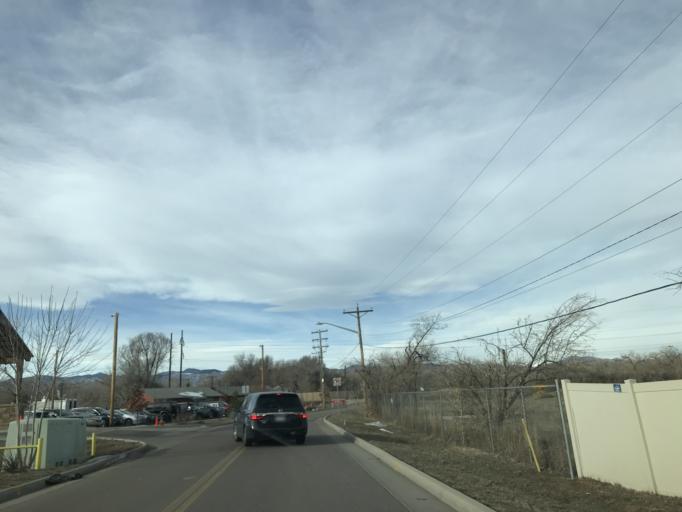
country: US
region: Colorado
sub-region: Arapahoe County
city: Columbine Valley
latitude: 39.5943
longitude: -105.0244
